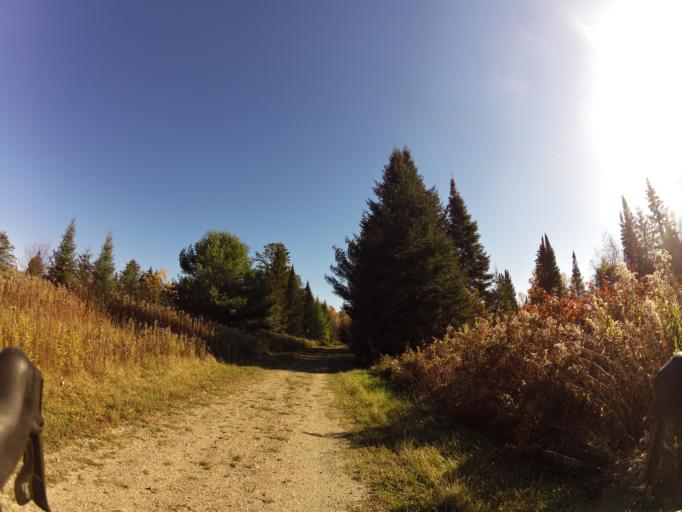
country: CA
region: Quebec
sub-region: Outaouais
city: Wakefield
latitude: 45.8191
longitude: -75.9670
